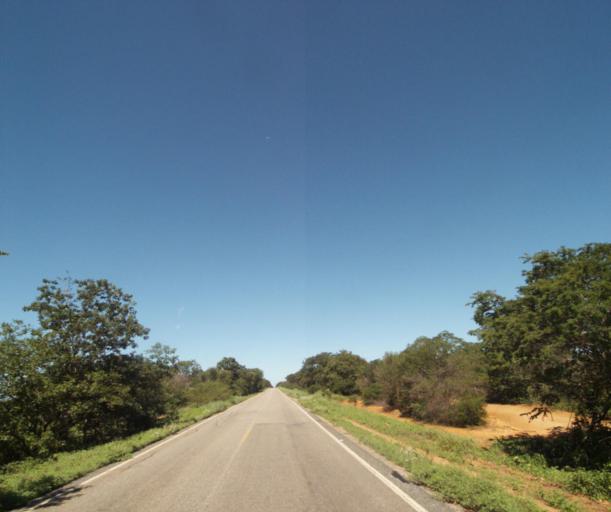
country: BR
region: Bahia
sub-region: Palmas De Monte Alto
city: Palmas de Monte Alto
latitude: -14.2609
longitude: -43.3028
